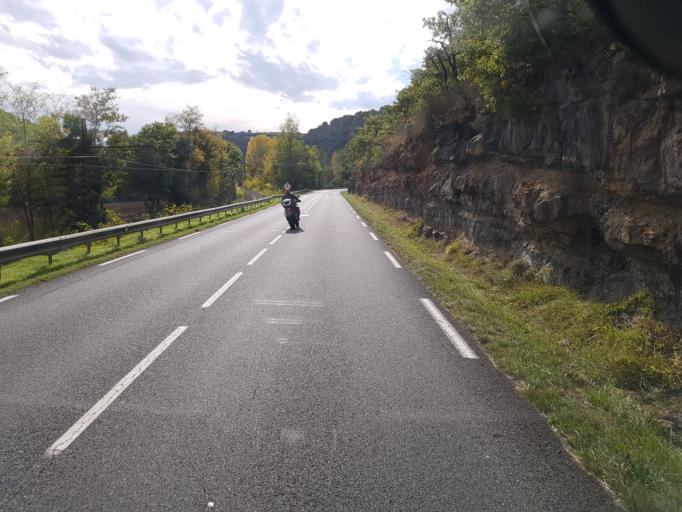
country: FR
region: Midi-Pyrenees
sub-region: Departement de l'Aveyron
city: Saint-Georges-de-Luzencon
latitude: 44.0388
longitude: 2.9652
